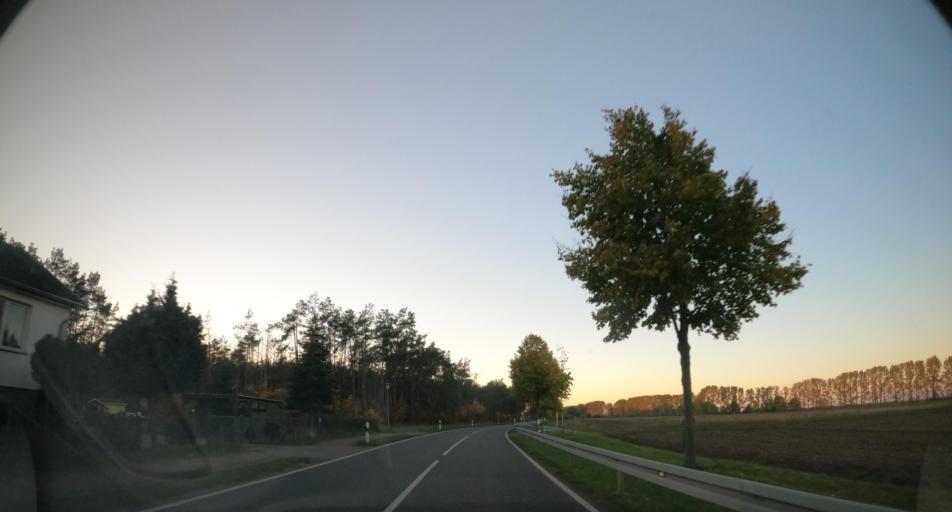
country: DE
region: Mecklenburg-Vorpommern
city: Ueckermunde
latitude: 53.7630
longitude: 13.9976
